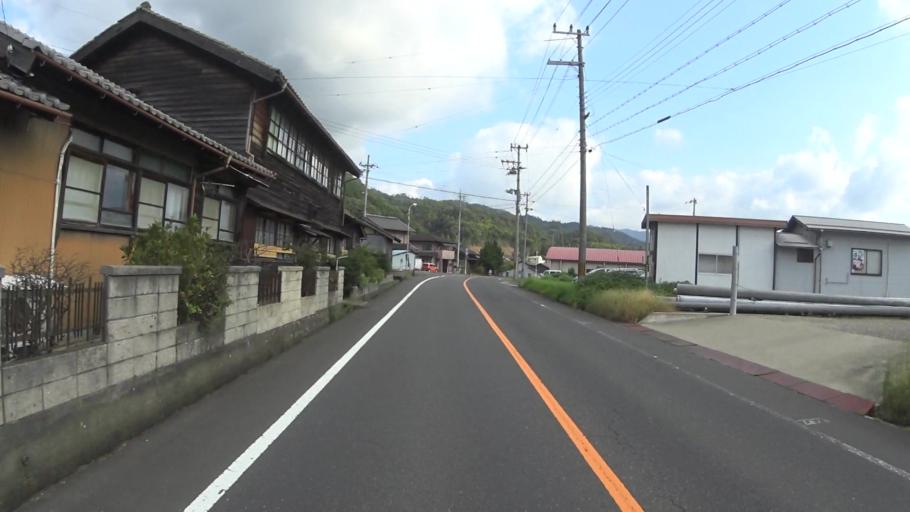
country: JP
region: Kyoto
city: Miyazu
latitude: 35.5552
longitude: 135.1392
